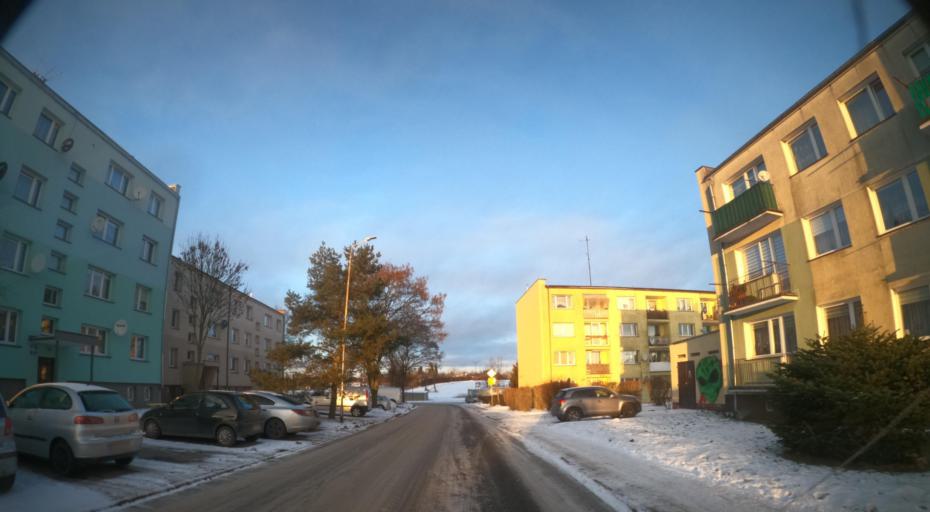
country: PL
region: West Pomeranian Voivodeship
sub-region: Powiat koszalinski
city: Sianow
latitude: 54.2334
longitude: 16.3082
